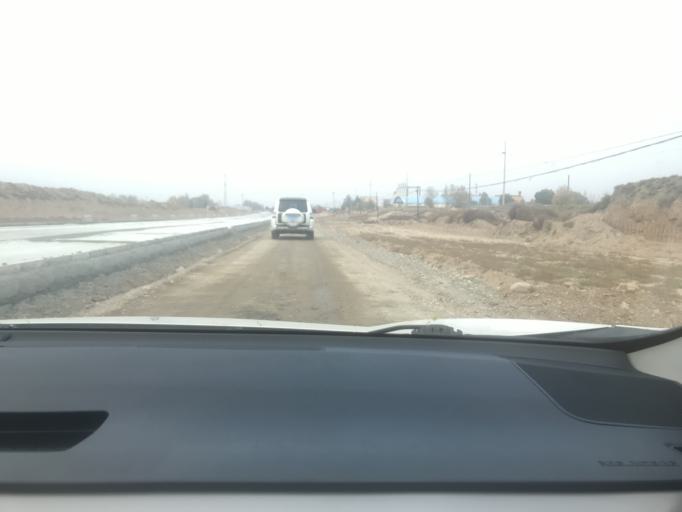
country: CN
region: Gansu Sheng
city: Gulang
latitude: 37.5115
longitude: 102.9011
